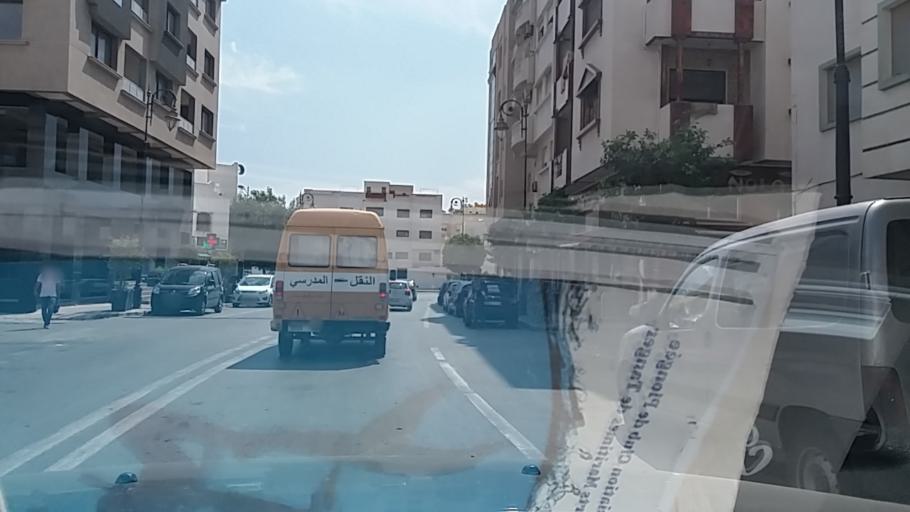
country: MA
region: Tanger-Tetouan
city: Tetouan
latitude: 35.5761
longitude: -5.3431
